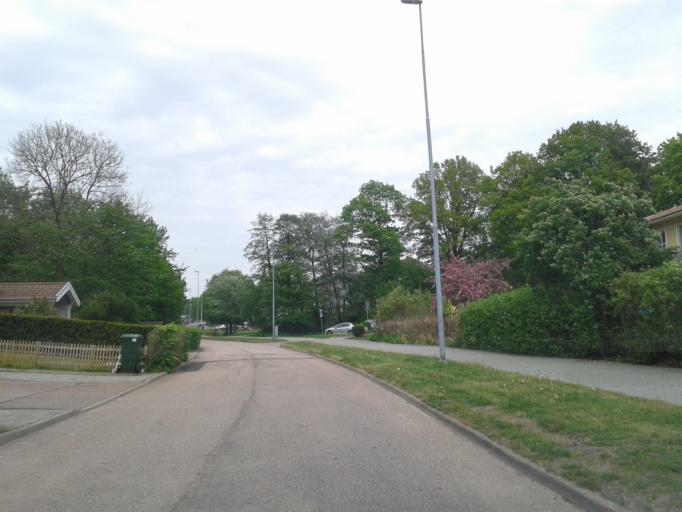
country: SE
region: Vaestra Goetaland
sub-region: Kungalvs Kommun
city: Kungalv
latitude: 57.8841
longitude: 11.9527
